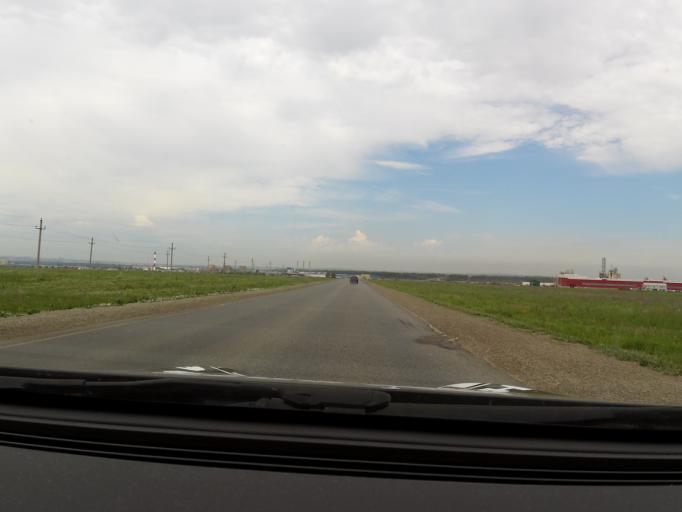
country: RU
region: Bashkortostan
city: Iglino
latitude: 54.7573
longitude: 56.2782
